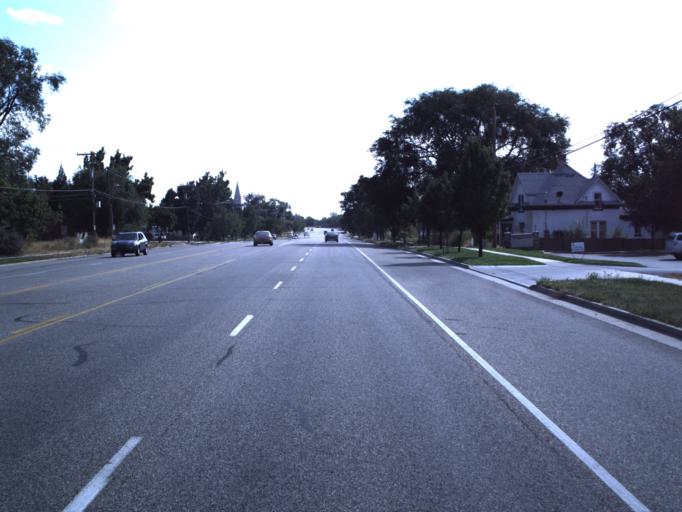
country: US
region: Utah
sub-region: Box Elder County
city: Perry
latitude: 41.4675
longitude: -112.0316
